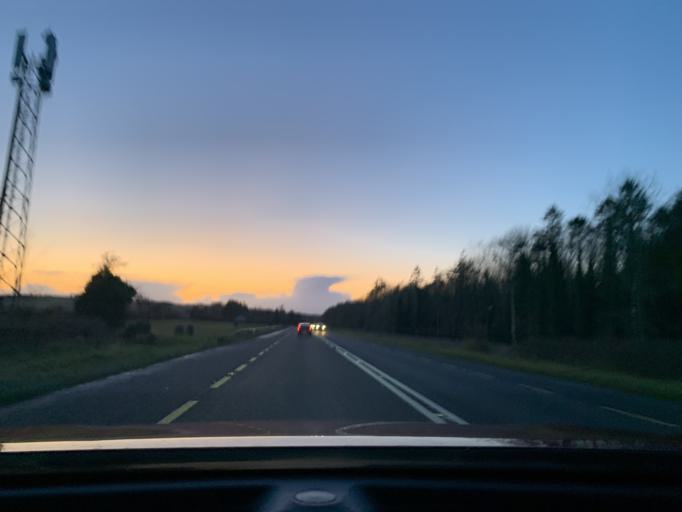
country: IE
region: Connaught
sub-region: Roscommon
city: Boyle
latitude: 53.9703
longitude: -8.2088
